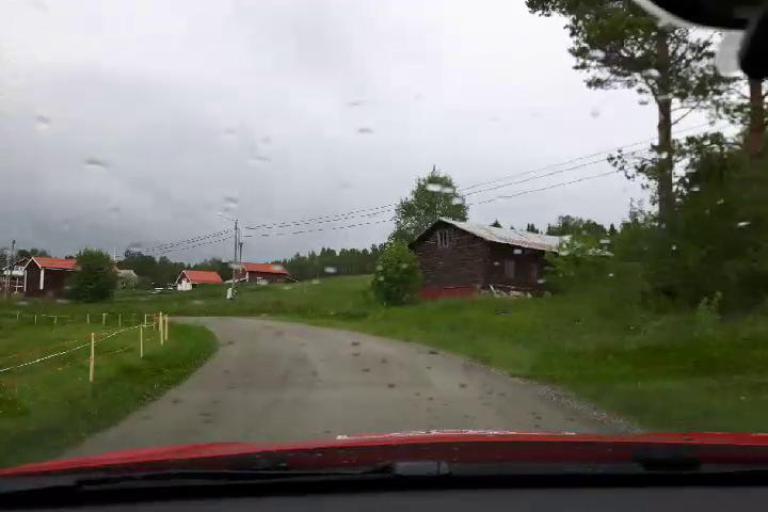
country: SE
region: Jaemtland
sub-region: Bergs Kommun
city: Hoverberg
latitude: 62.7364
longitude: 14.4548
